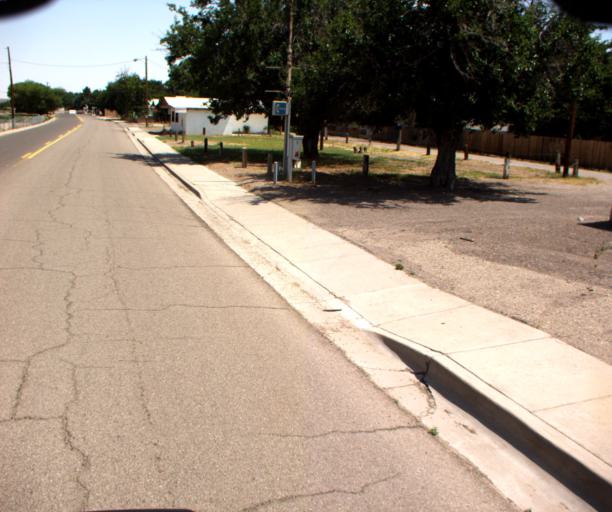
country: US
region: Arizona
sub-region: Greenlee County
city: Clifton
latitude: 32.7240
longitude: -109.1066
